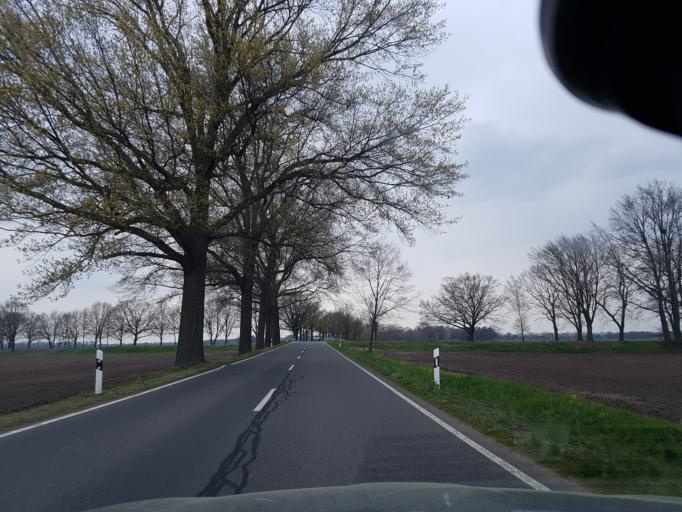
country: DE
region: Brandenburg
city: Schraden
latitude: 51.4026
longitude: 13.7000
